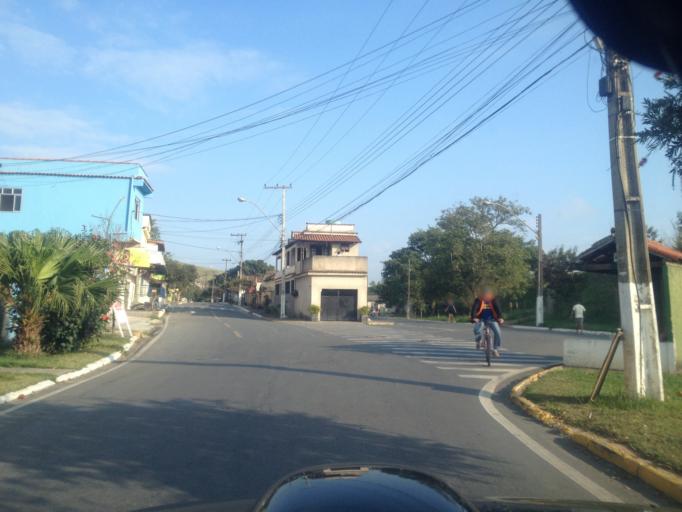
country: BR
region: Rio de Janeiro
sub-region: Porto Real
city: Porto Real
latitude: -22.4499
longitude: -44.3061
